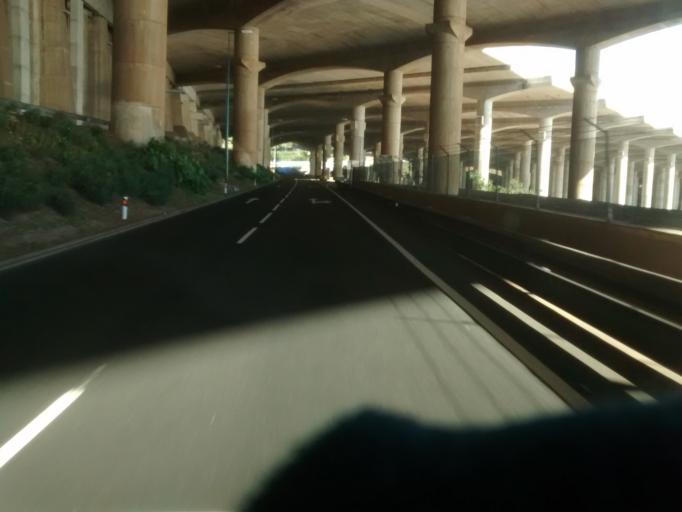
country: PT
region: Madeira
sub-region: Machico
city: Machico
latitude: 32.6989
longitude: -16.7710
